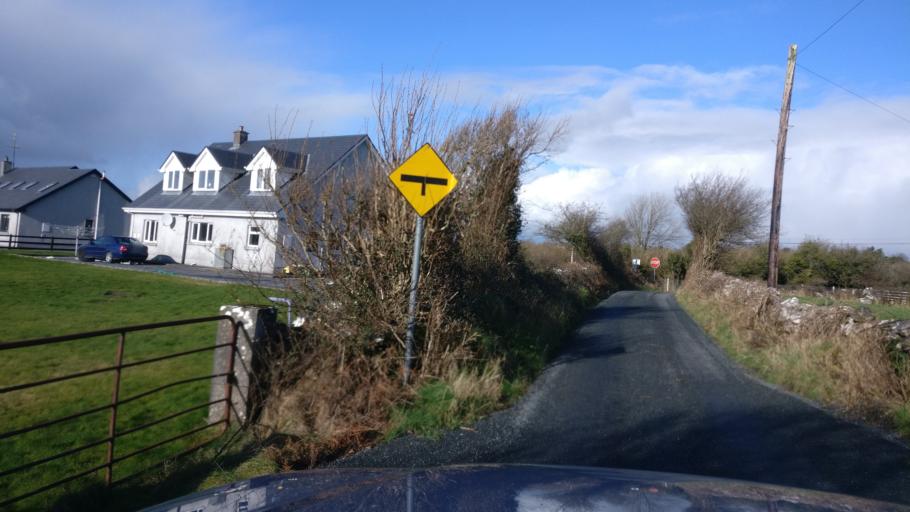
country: IE
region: Connaught
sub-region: County Galway
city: Athenry
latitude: 53.2410
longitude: -8.7760
